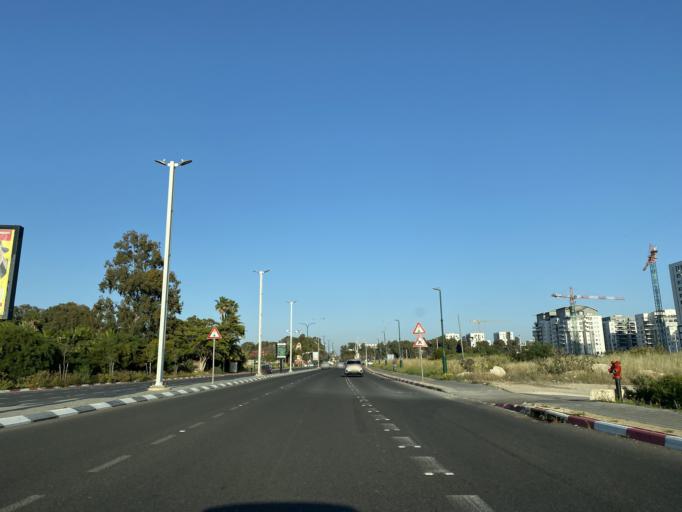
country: IL
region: Tel Aviv
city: Kefar Shemaryahu
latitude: 32.1786
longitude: 34.8280
